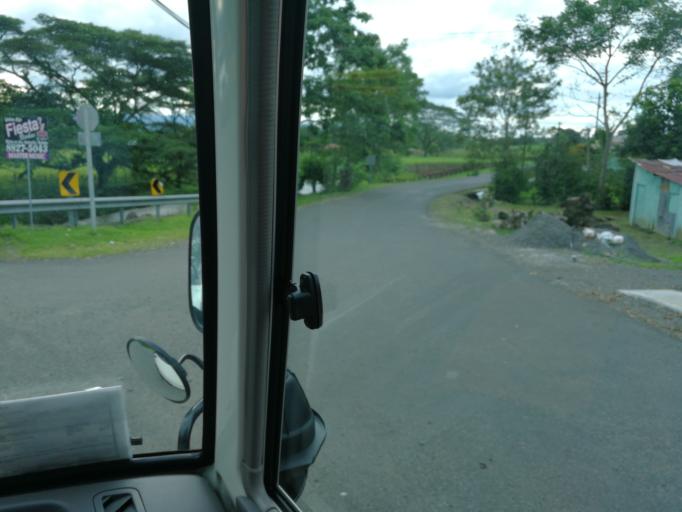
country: CR
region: Alajuela
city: Quesada
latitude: 10.3634
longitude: -84.5019
